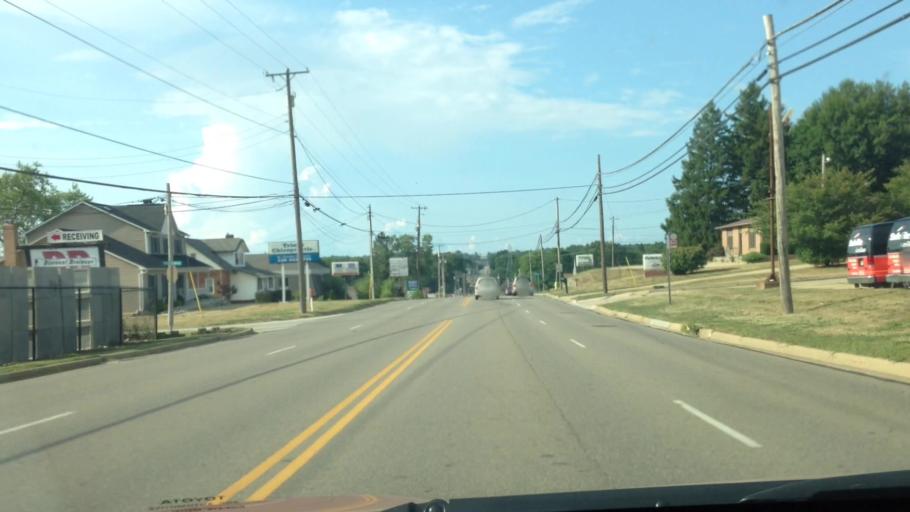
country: US
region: Ohio
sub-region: Summit County
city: Portage Lakes
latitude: 41.0015
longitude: -81.4921
